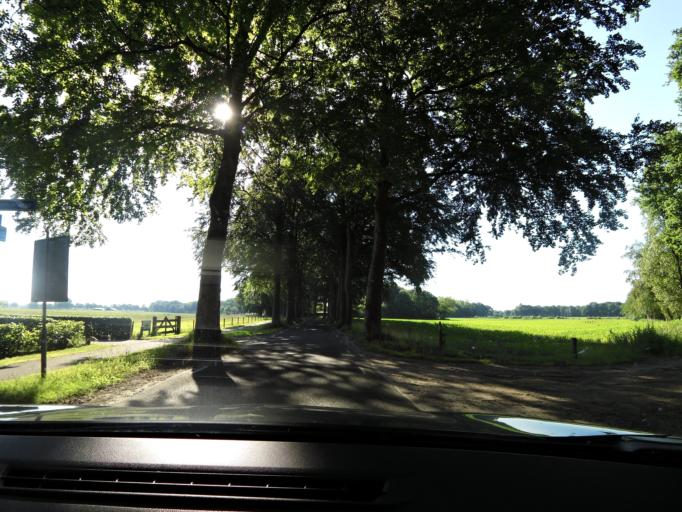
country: NL
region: Overijssel
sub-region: Gemeente Deventer
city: Schalkhaar
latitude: 52.2724
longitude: 6.2453
